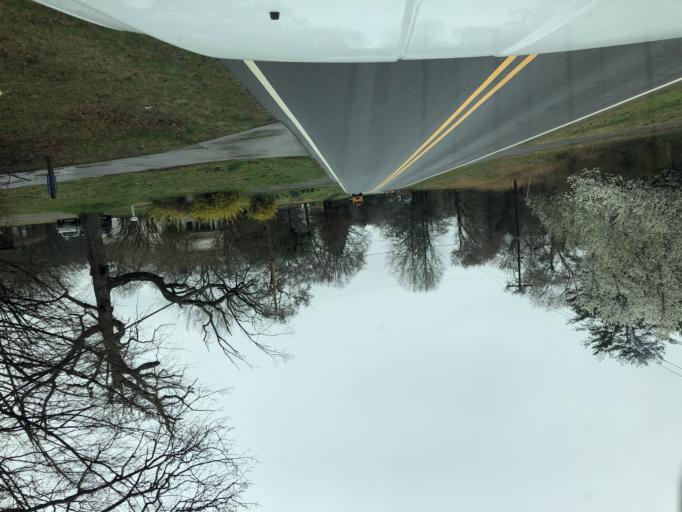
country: US
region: North Carolina
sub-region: Gaston County
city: Mount Holly
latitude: 35.3356
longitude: -80.9195
